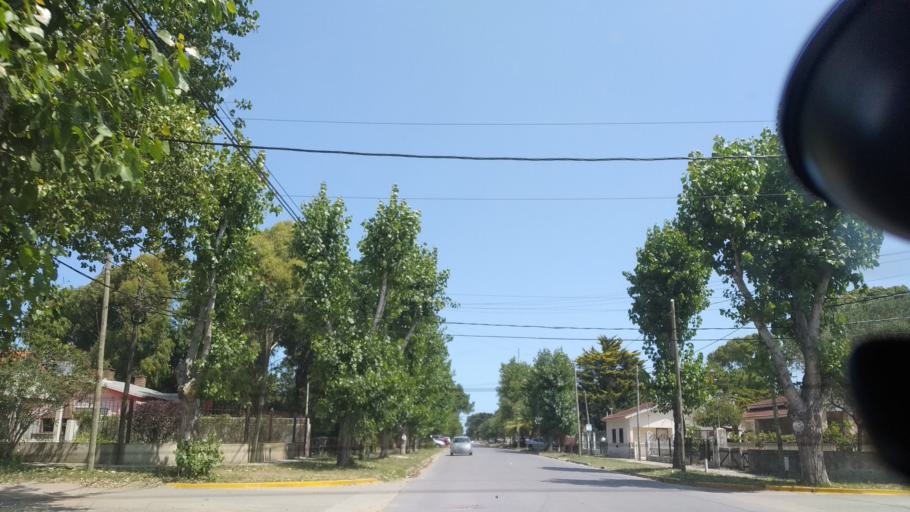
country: AR
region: Buenos Aires
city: Mar del Tuyu
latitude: -36.5730
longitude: -56.6939
